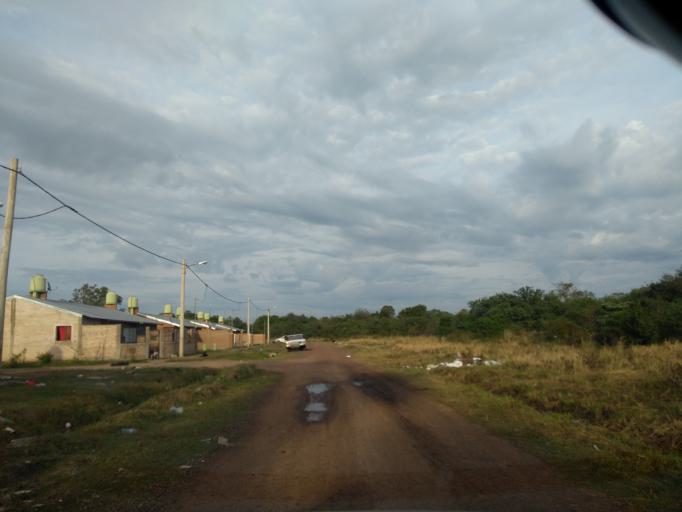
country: AR
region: Chaco
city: Fontana
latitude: -27.4232
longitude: -59.0496
